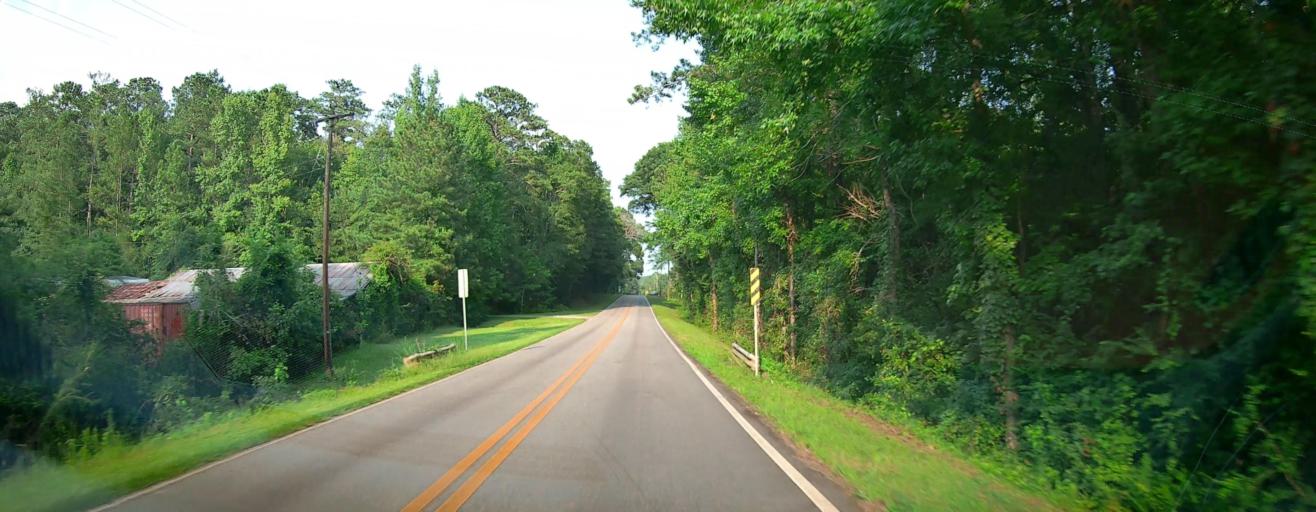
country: US
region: Georgia
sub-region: Monroe County
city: Forsyth
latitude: 33.1064
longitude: -83.8045
